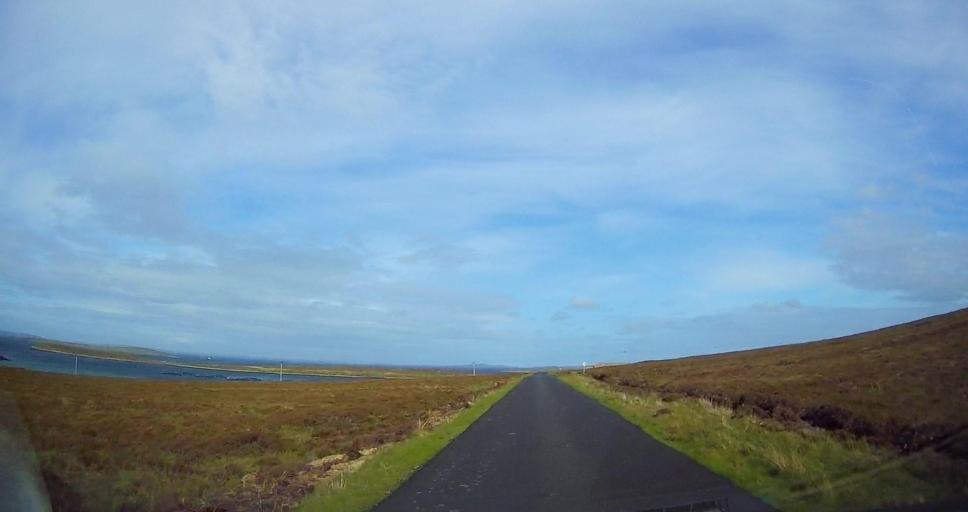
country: GB
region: Scotland
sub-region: Orkney Islands
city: Stromness
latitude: 58.8589
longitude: -3.2221
